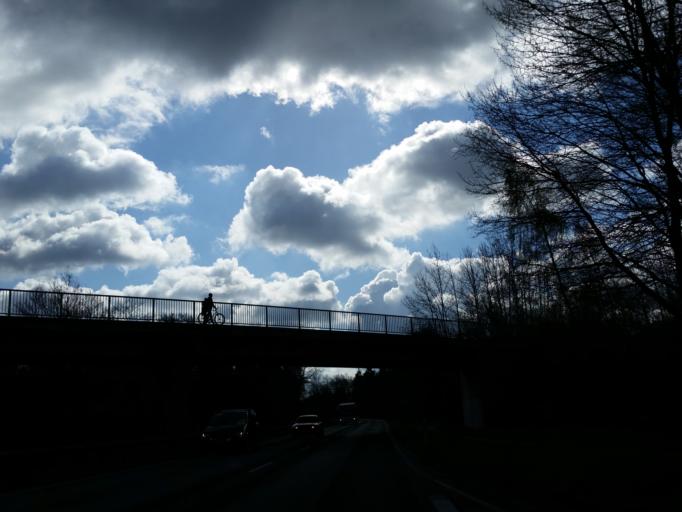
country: DE
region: Lower Saxony
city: Rotenburg
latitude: 53.1219
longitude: 9.3770
